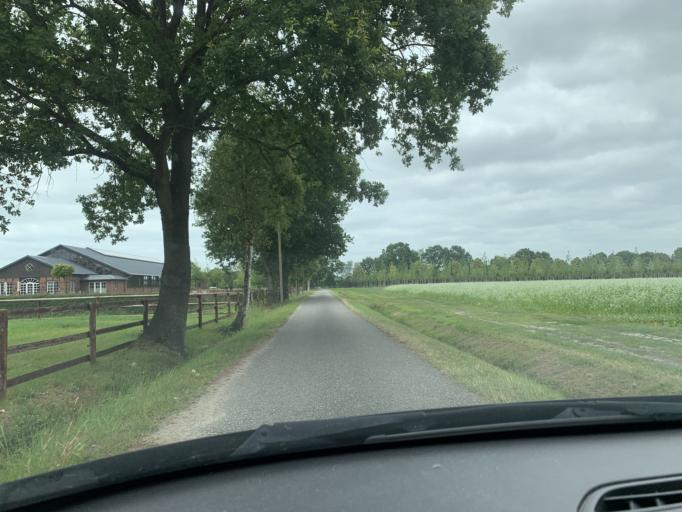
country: DE
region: Lower Saxony
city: Westerstede
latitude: 53.2259
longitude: 7.9691
